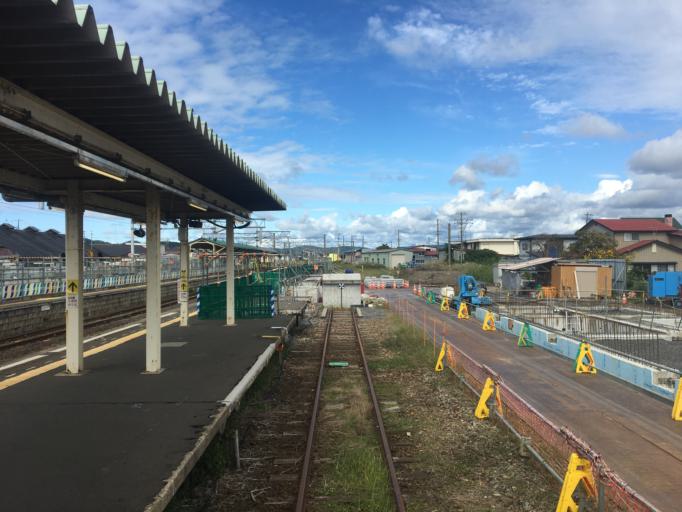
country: JP
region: Akita
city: Akita Shi
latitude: 39.3864
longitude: 140.0577
